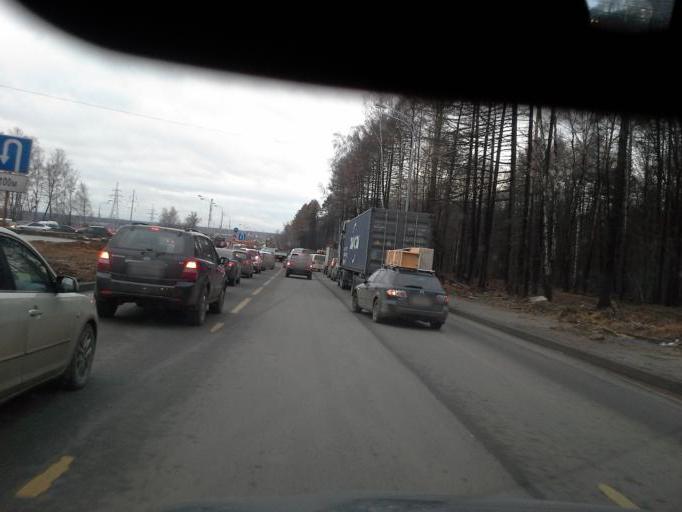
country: RU
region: Moskovskaya
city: Kommunarka
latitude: 55.5792
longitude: 37.4639
